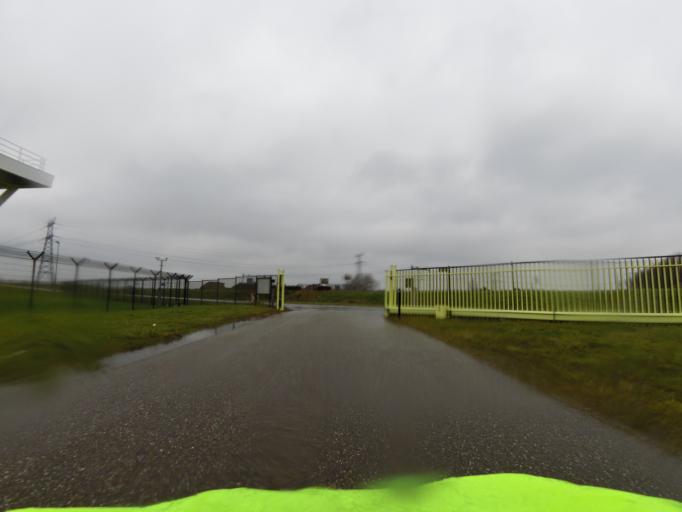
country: NL
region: South Holland
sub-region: Gemeente Rotterdam
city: Hoek van Holland
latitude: 51.9573
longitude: 4.1673
